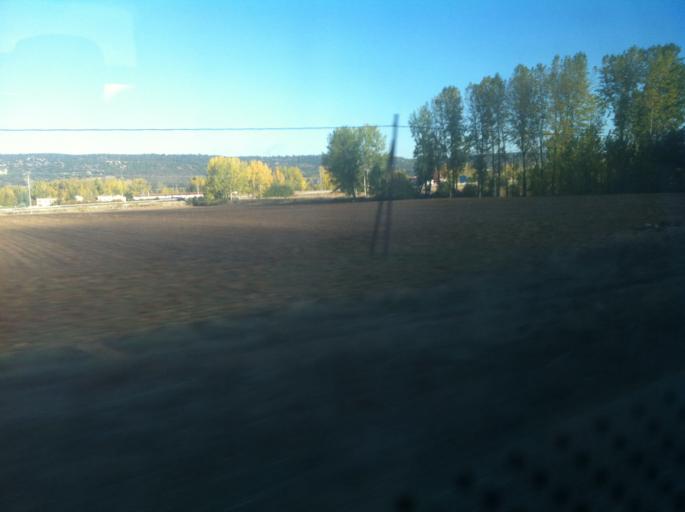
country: ES
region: Castille and Leon
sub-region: Provincia de Palencia
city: Quintana del Puente
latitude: 42.0690
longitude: -4.2158
